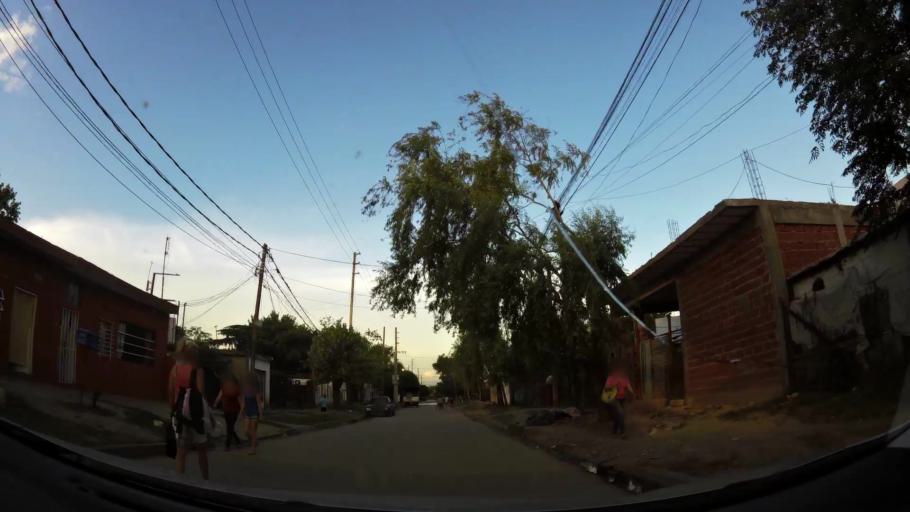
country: AR
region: Buenos Aires
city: Santa Catalina - Dique Lujan
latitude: -34.4344
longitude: -58.6678
